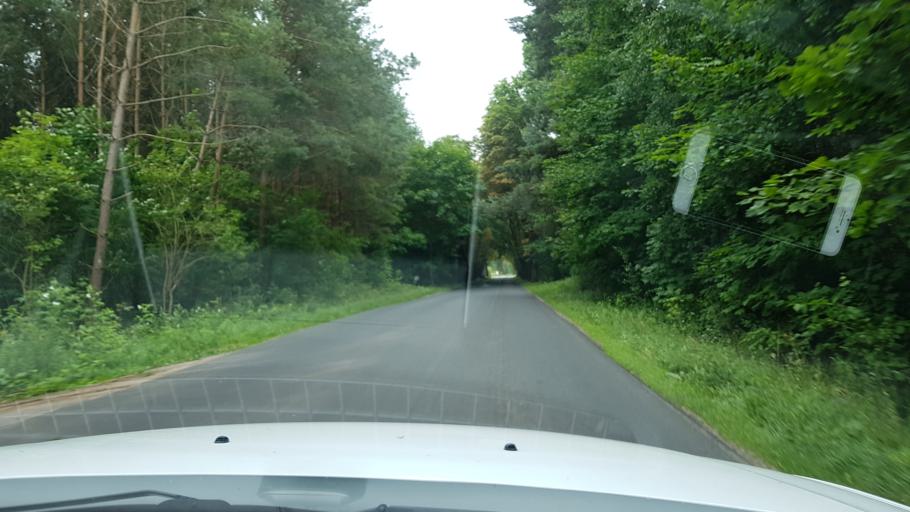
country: PL
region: West Pomeranian Voivodeship
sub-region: Powiat slawienski
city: Slawno
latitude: 54.4966
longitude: 16.5769
